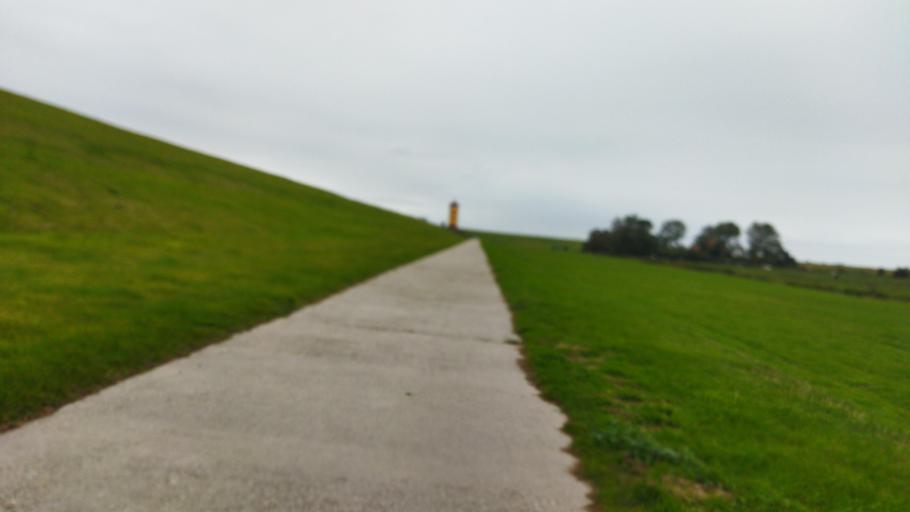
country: DE
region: Lower Saxony
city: Wirdum
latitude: 53.4953
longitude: 7.0439
